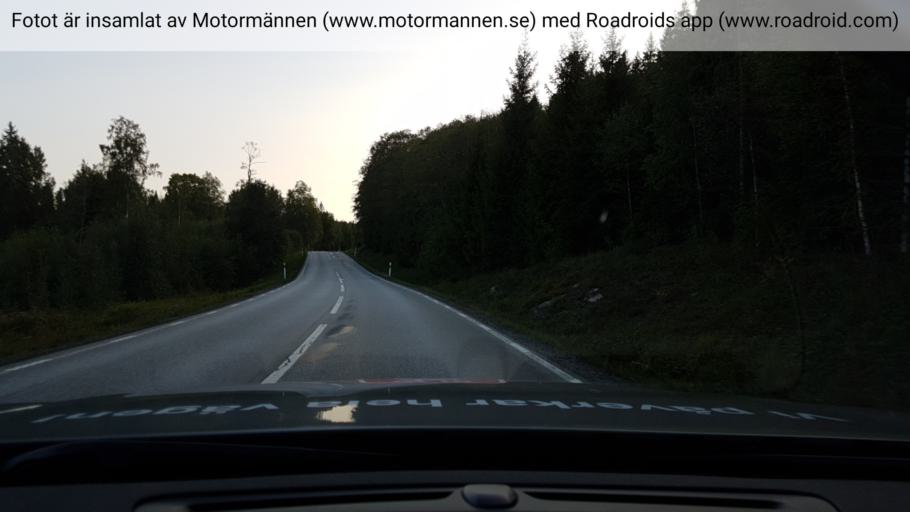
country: SE
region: OErebro
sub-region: Ljusnarsbergs Kommun
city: Kopparberg
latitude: 59.8202
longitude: 14.9644
